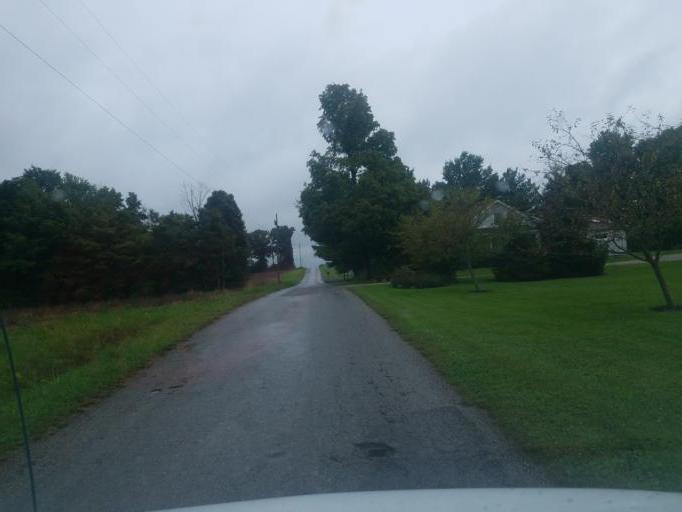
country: US
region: Ohio
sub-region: Wayne County
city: West Salem
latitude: 40.9372
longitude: -82.1378
